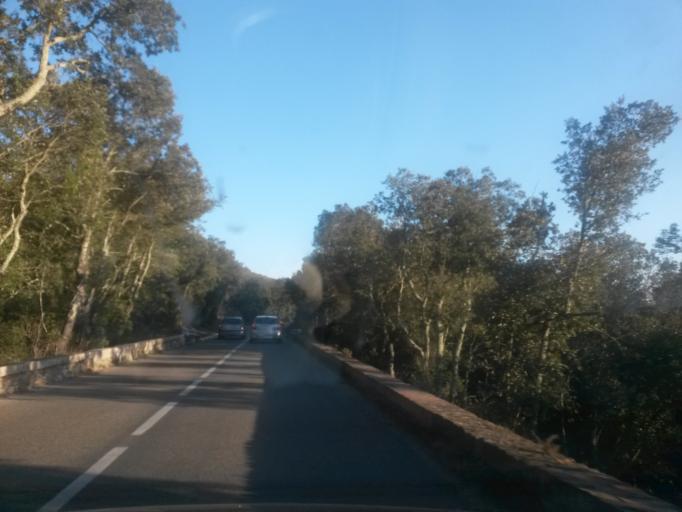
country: ES
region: Catalonia
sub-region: Provincia de Girona
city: Macanet de Cabrenys
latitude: 42.3883
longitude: 2.7822
